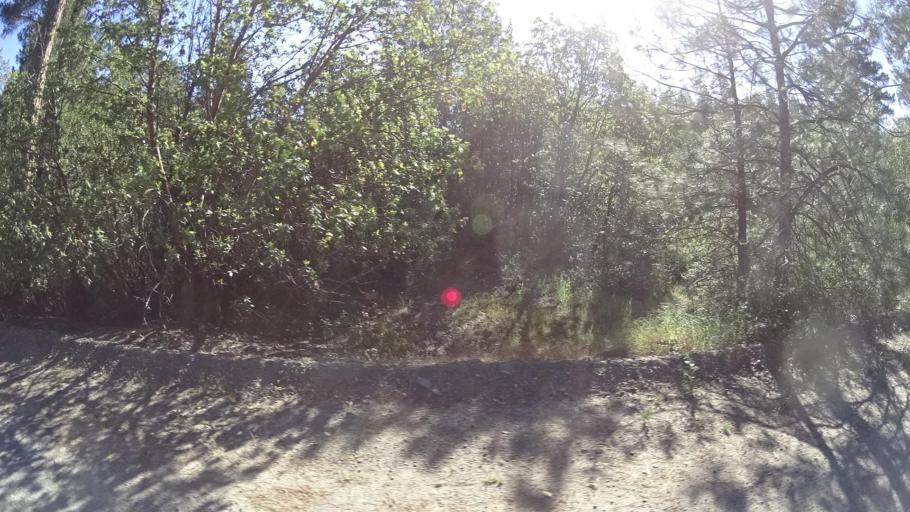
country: US
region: California
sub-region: Lake County
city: Upper Lake
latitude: 39.4048
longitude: -122.9717
